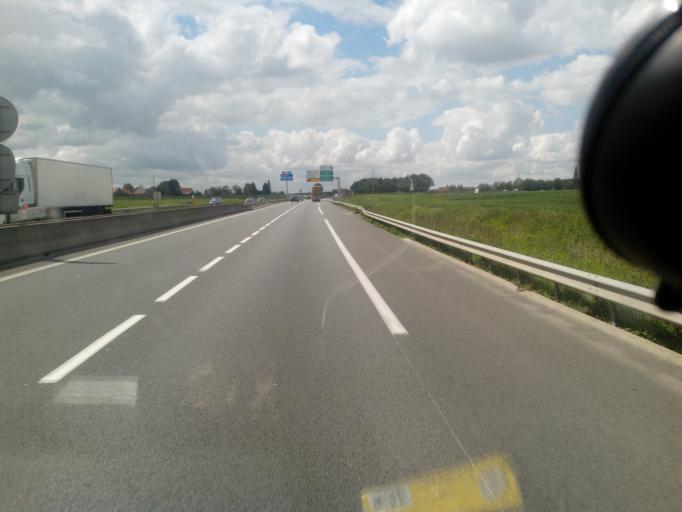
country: FR
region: Nord-Pas-de-Calais
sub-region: Departement du Nord
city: Meteren
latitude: 50.7307
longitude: 2.7048
